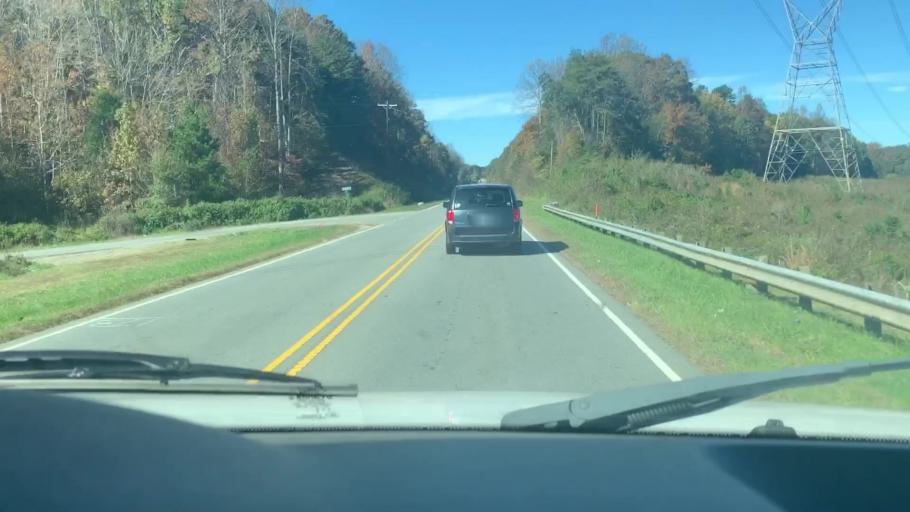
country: US
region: North Carolina
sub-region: Lincoln County
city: Lowesville
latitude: 35.4303
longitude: -80.9648
